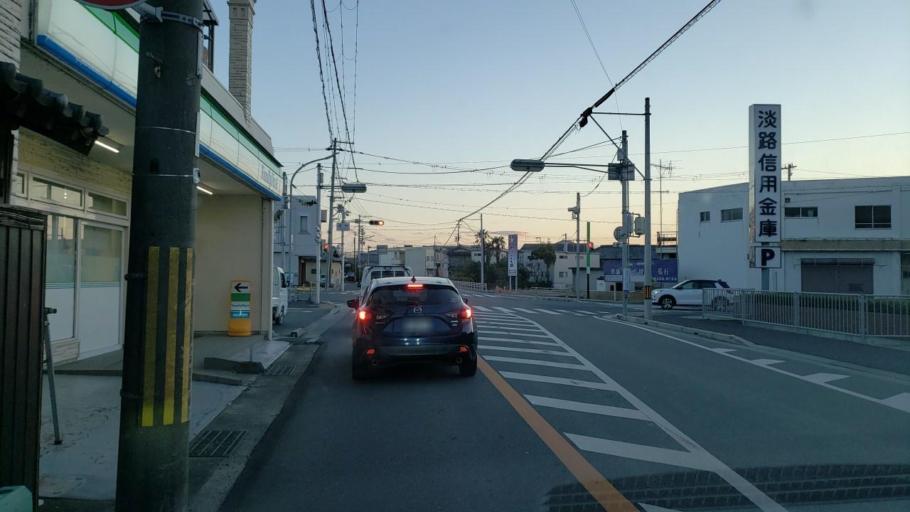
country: JP
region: Hyogo
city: Fukura
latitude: 34.3231
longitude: 134.7726
